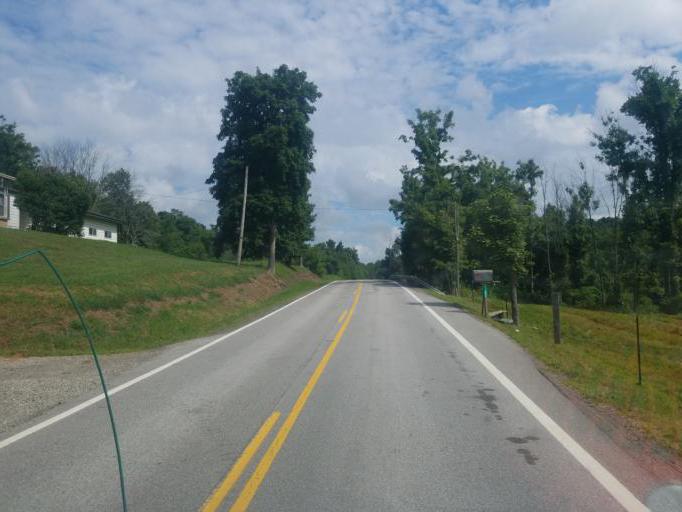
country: US
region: Ohio
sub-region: Belmont County
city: Barnesville
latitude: 40.0599
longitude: -81.3258
